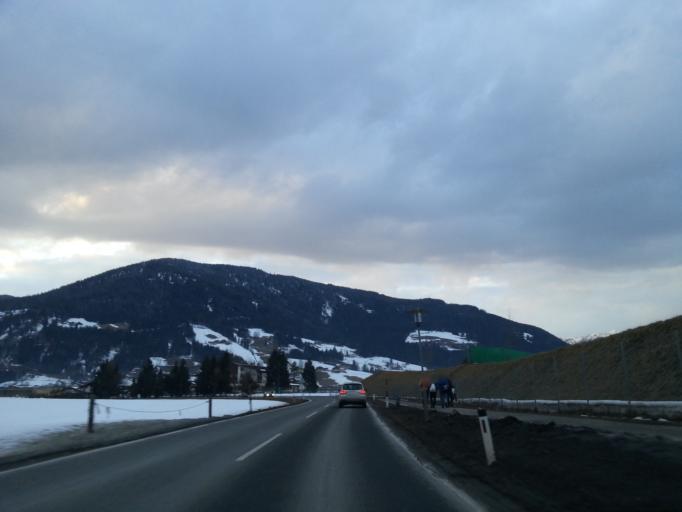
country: AT
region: Salzburg
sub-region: Politischer Bezirk Sankt Johann im Pongau
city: Altenmarkt im Pongau
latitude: 47.3809
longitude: 13.4072
